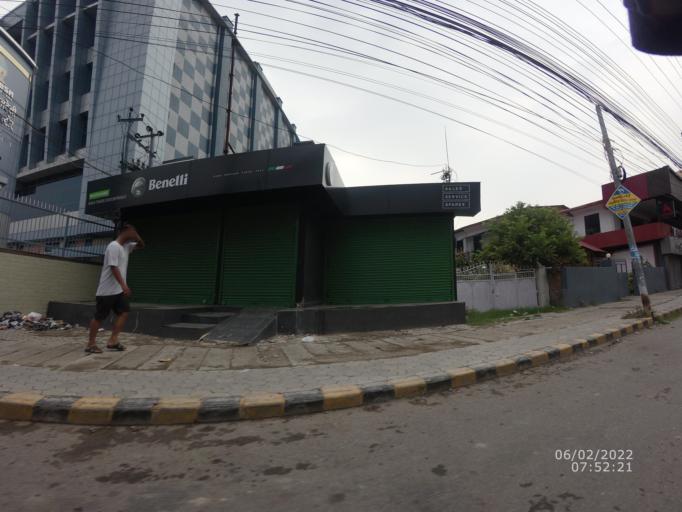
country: NP
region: Western Region
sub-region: Lumbini Zone
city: Bhairahawa
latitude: 27.5129
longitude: 83.4543
